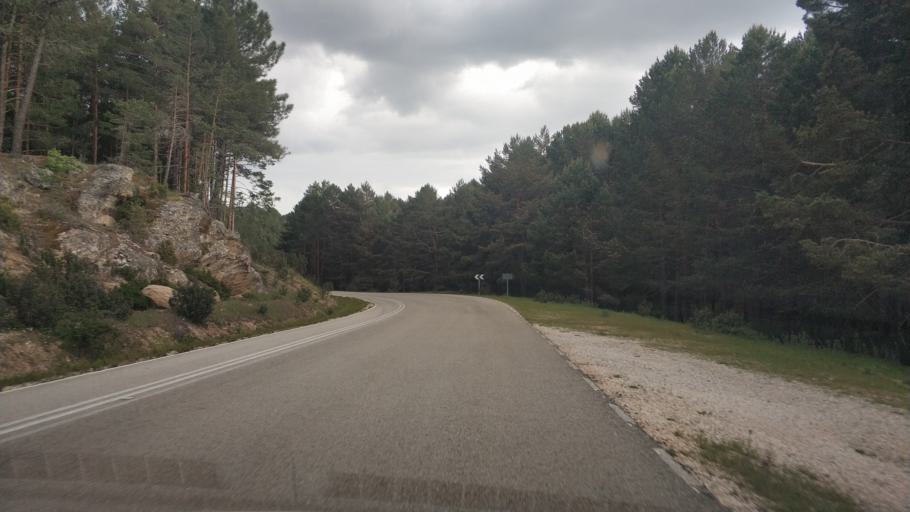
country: ES
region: Castille and Leon
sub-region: Provincia de Soria
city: San Leonardo de Yague
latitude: 41.8480
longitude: -3.0698
